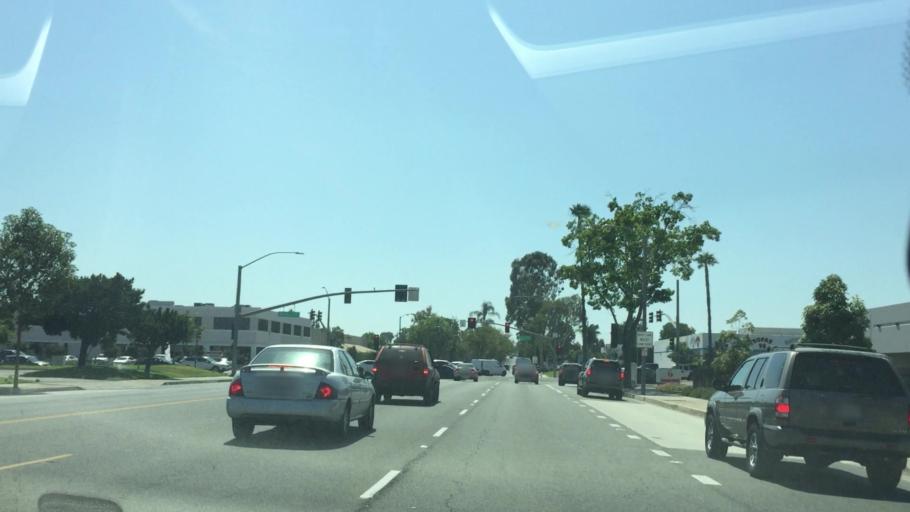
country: US
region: California
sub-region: Orange County
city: Fountain Valley
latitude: 33.7087
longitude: -117.9187
